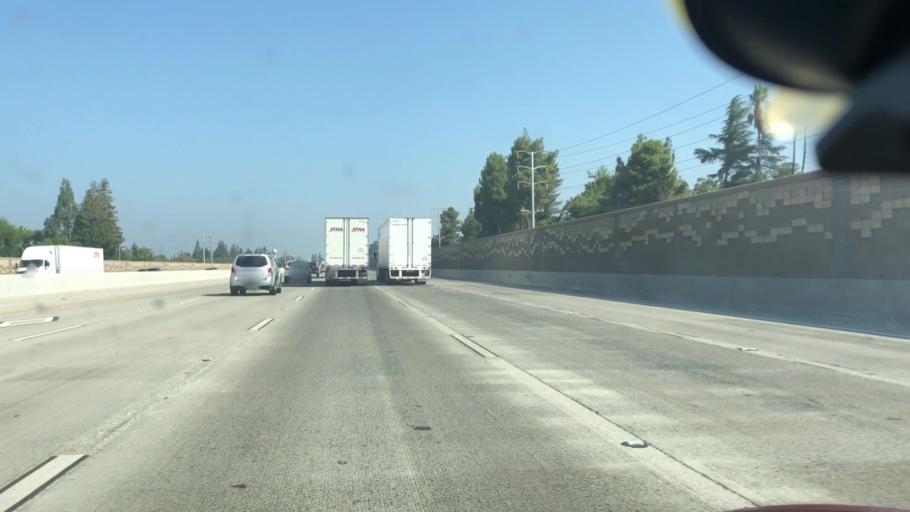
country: US
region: California
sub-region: San Joaquin County
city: Country Club
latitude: 37.9891
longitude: -121.3450
